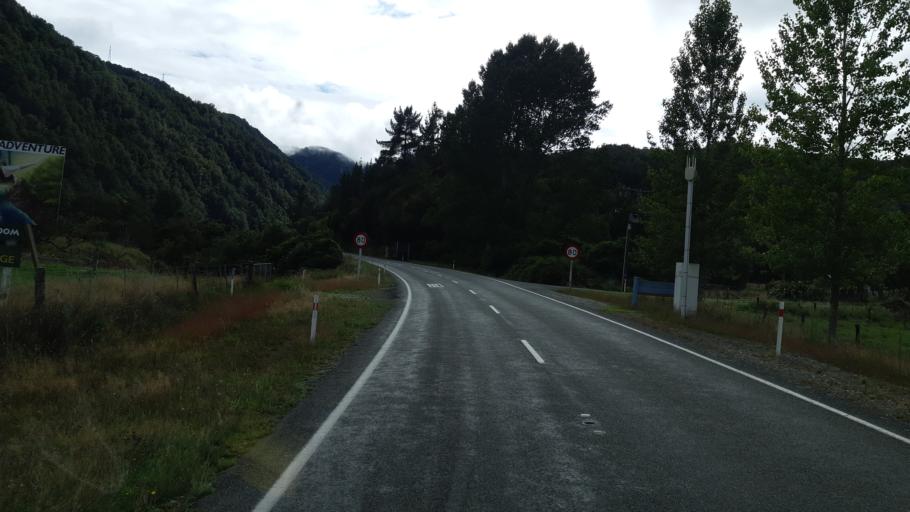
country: NZ
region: West Coast
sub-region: Buller District
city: Westport
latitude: -41.7815
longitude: 172.2163
